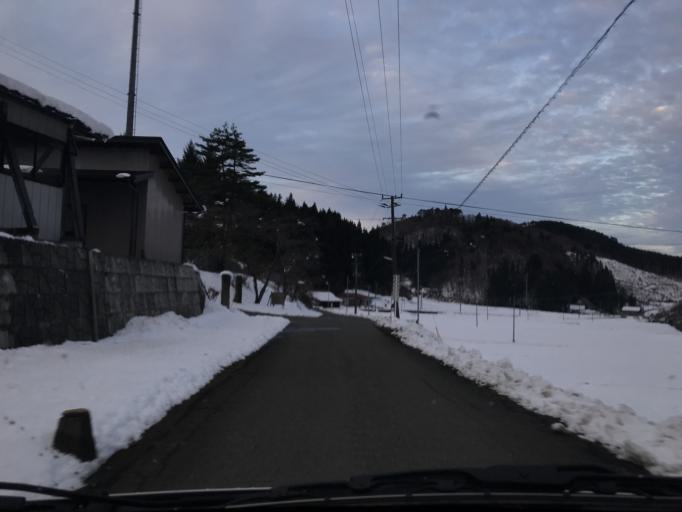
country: JP
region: Iwate
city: Mizusawa
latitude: 39.0442
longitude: 141.0120
